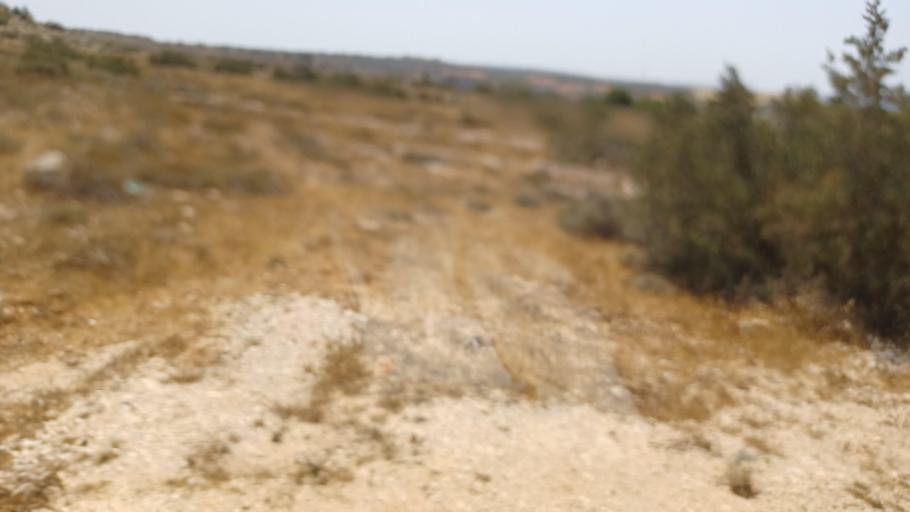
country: CY
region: Ammochostos
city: Paralimni
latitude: 35.0074
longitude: 33.9688
